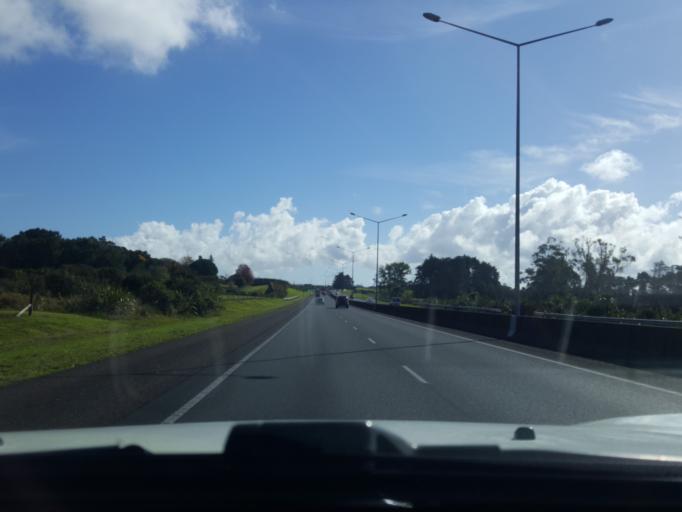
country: NZ
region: Auckland
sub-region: Auckland
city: Rosebank
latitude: -36.8017
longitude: 174.6021
